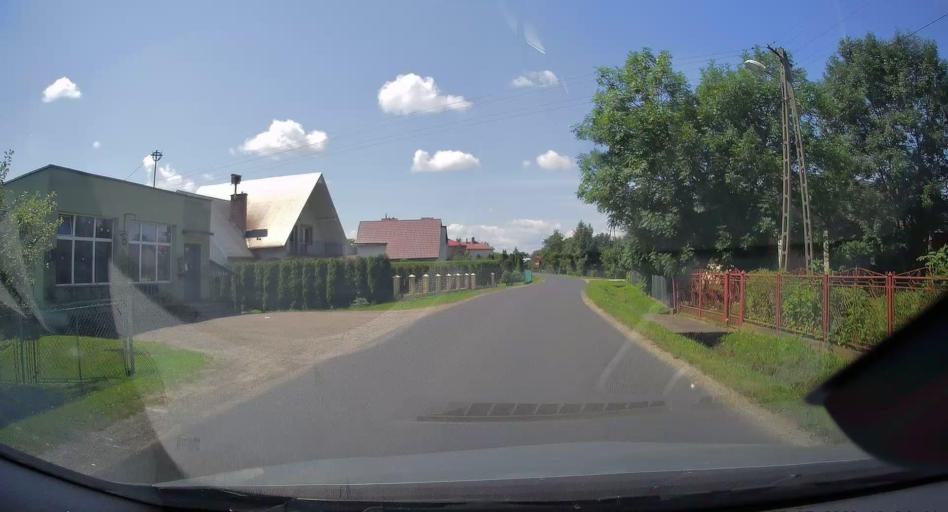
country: PL
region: Subcarpathian Voivodeship
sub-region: Powiat przemyski
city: Medyka
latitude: 49.8348
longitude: 22.8794
